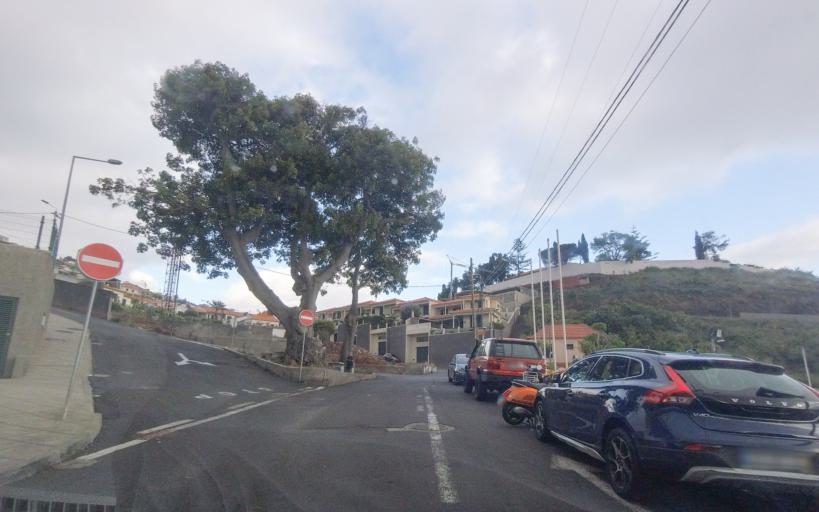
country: PT
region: Madeira
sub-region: Funchal
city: Funchal
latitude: 32.6481
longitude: -16.8807
